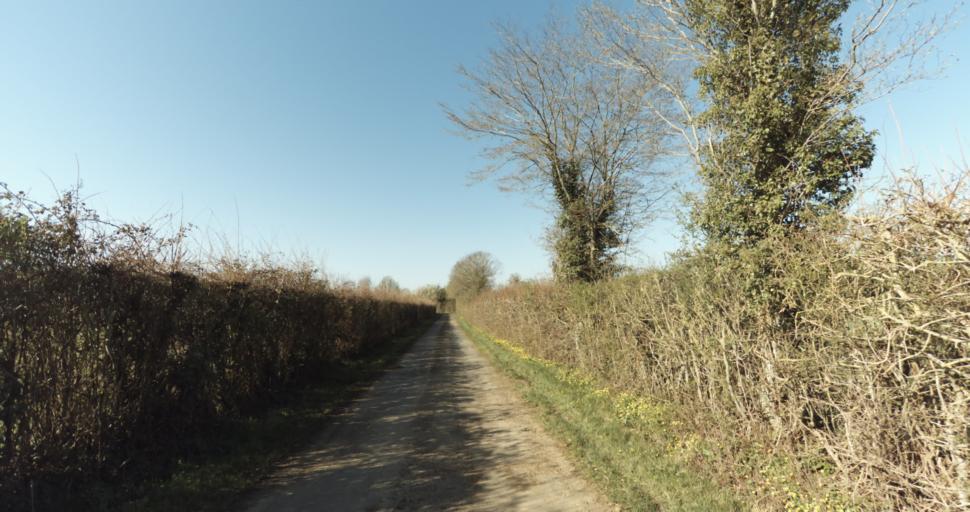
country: FR
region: Lower Normandy
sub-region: Departement du Calvados
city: Saint-Pierre-sur-Dives
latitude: 48.9604
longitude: 0.0205
